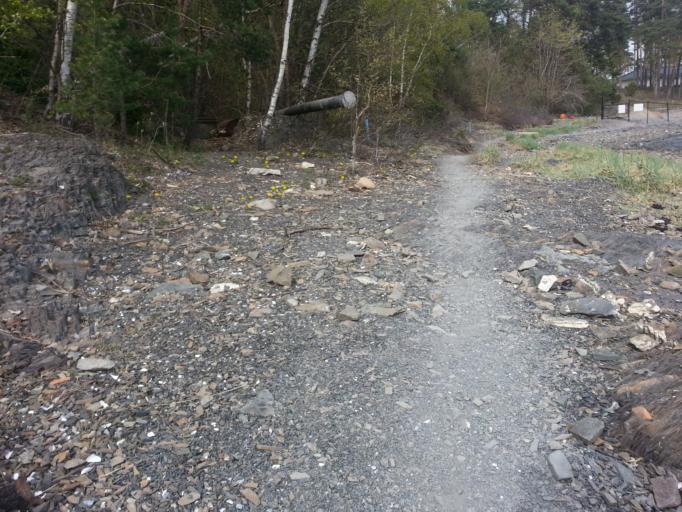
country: NO
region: Akershus
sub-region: Baerum
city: Lysaker
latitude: 59.9039
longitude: 10.6378
